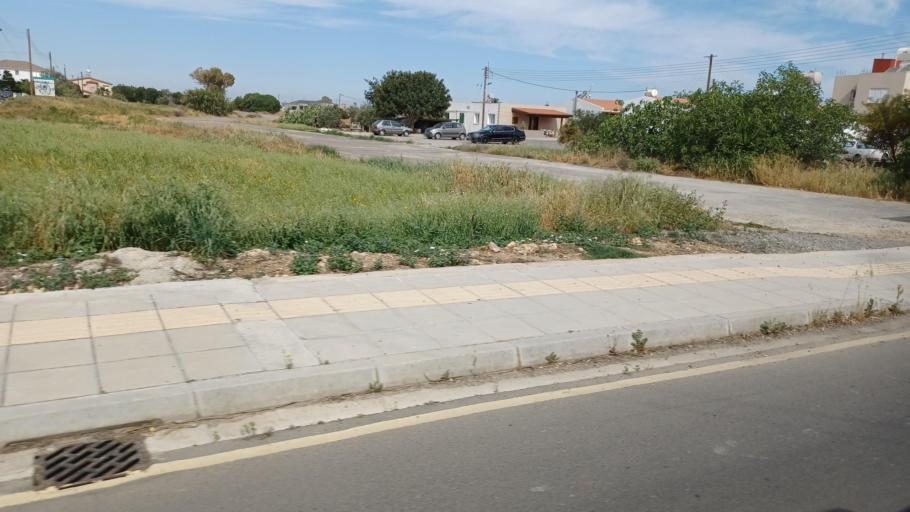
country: CY
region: Lefkosia
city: Kokkinotrimithia
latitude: 35.1571
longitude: 33.2053
